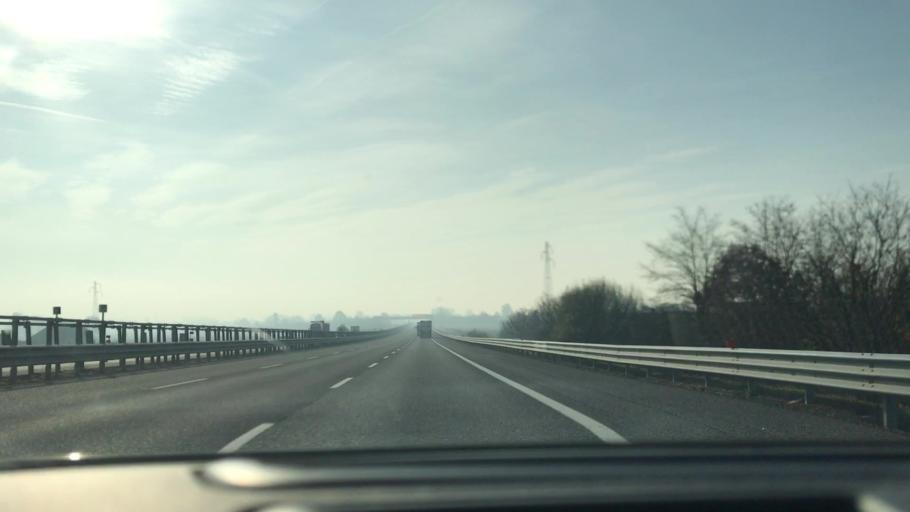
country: IT
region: Piedmont
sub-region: Provincia di Alessandria
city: Alessandria
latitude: 44.8947
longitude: 8.5685
